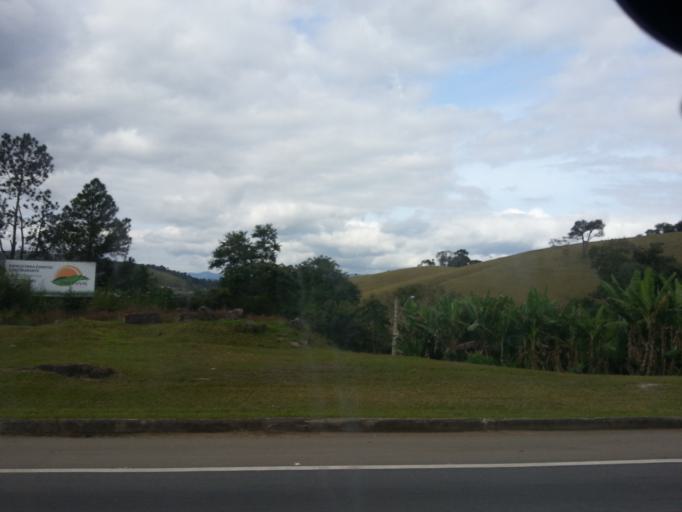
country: BR
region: Sao Paulo
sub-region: Santa Isabel
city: Santa Isabel
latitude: -23.3712
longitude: -46.2426
